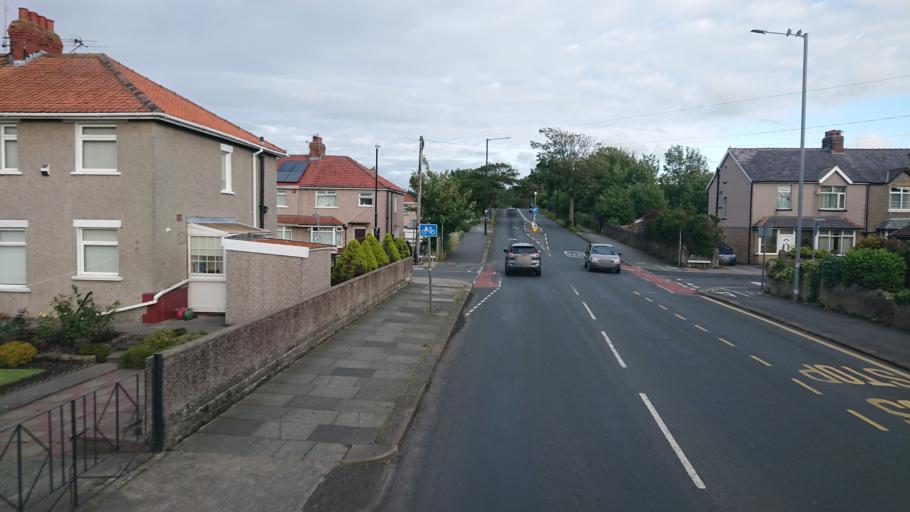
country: GB
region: England
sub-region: Lancashire
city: Morecambe
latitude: 54.0620
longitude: -2.8729
